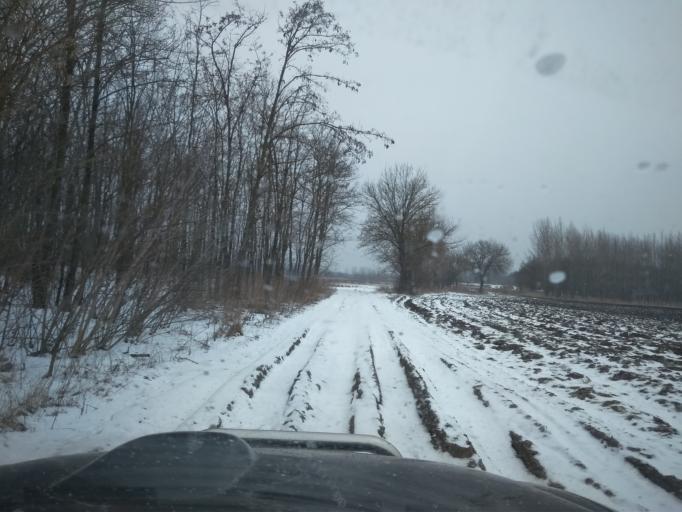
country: HU
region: Szabolcs-Szatmar-Bereg
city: Apagy
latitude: 47.9749
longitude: 21.9160
